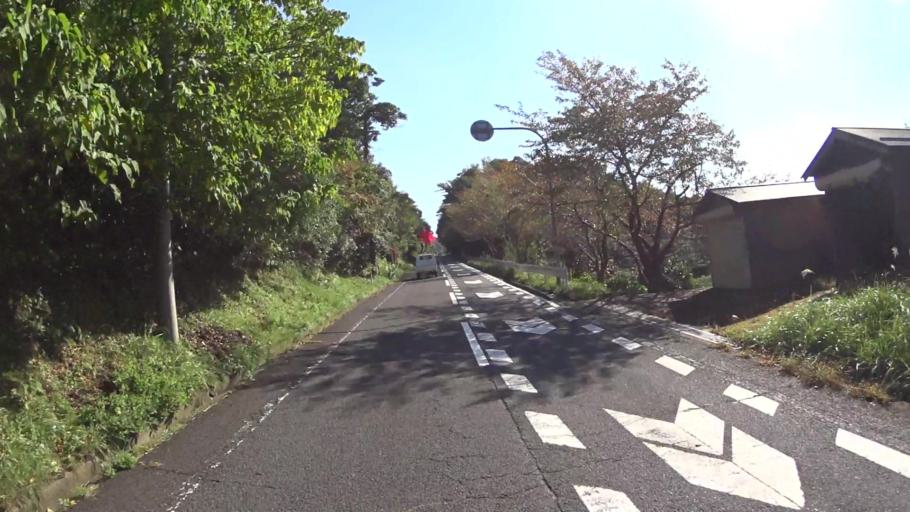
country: JP
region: Kyoto
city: Miyazu
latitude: 35.7106
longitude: 135.0696
